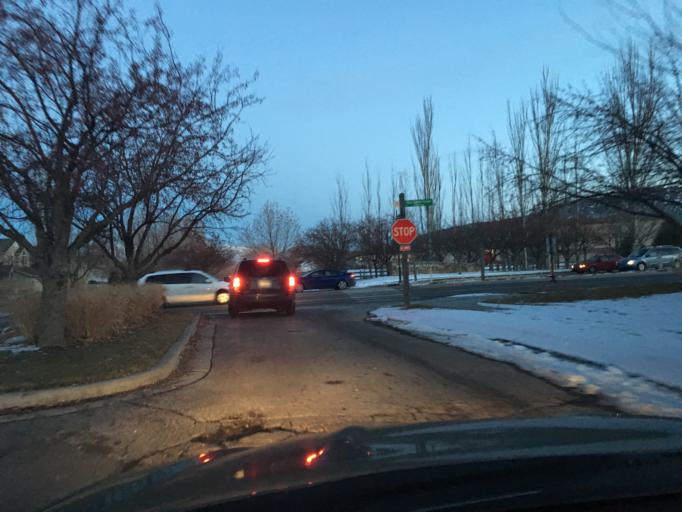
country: US
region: Utah
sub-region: Utah County
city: Eagle Mountain
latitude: 40.3604
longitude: -111.9861
